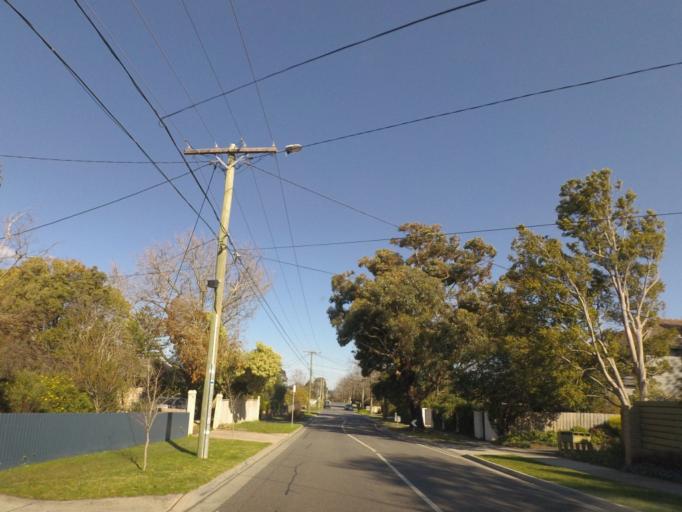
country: AU
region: Victoria
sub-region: Maroondah
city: Ringwood East
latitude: -37.8177
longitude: 145.2342
